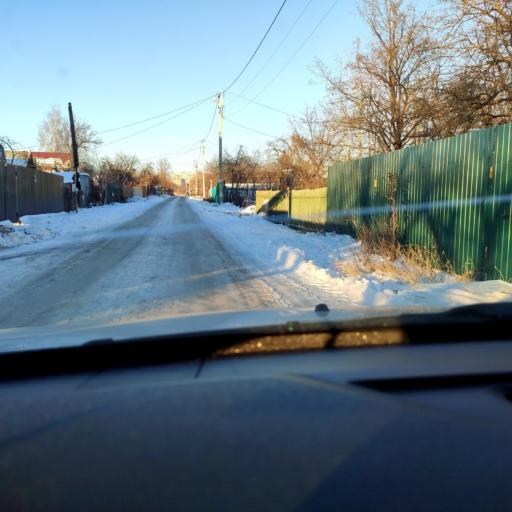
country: RU
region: Samara
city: Petra-Dubrava
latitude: 53.2849
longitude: 50.2916
